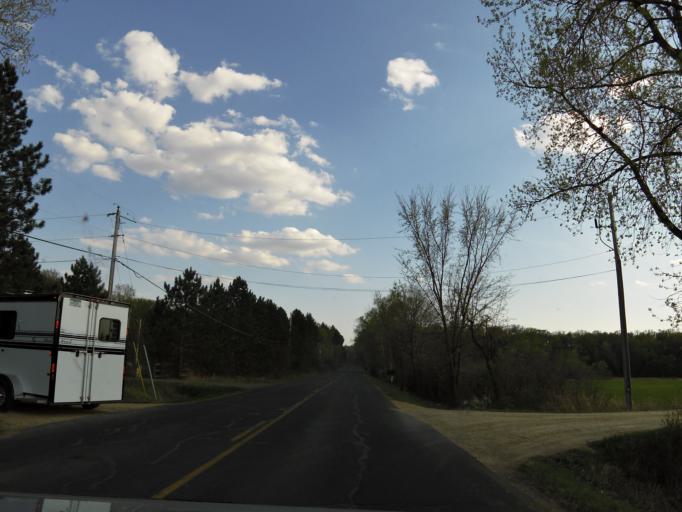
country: US
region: Minnesota
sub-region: Washington County
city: Lake Elmo
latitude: 44.9874
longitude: -92.8430
